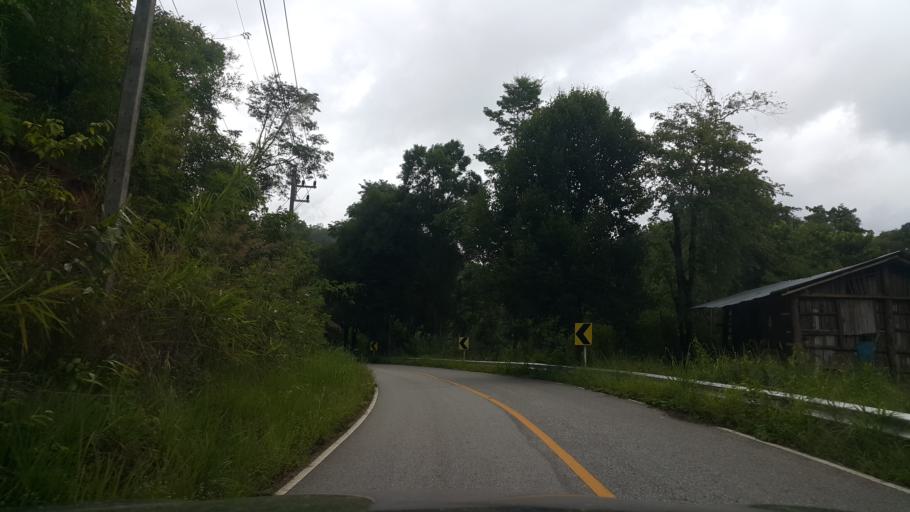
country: TH
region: Loei
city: Na Haeo
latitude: 17.5019
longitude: 100.8176
